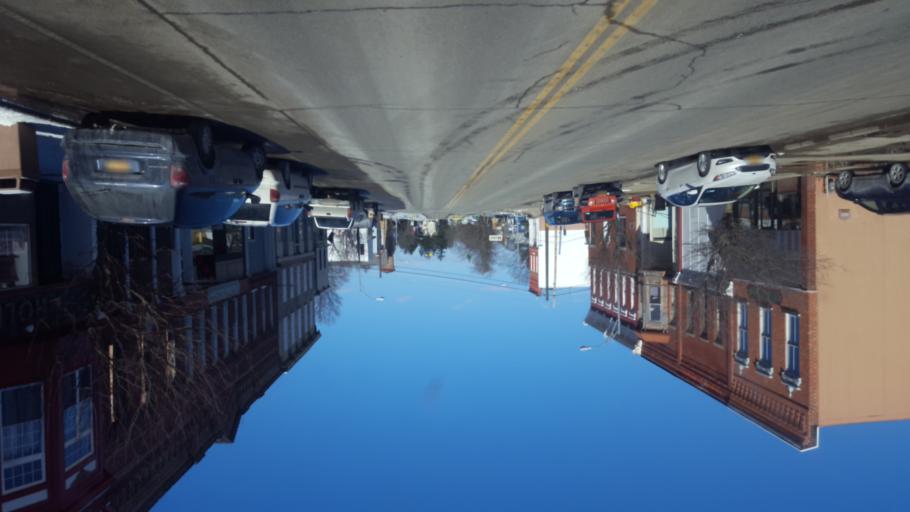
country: US
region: New York
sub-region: Allegany County
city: Friendship
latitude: 42.2077
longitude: -78.1345
